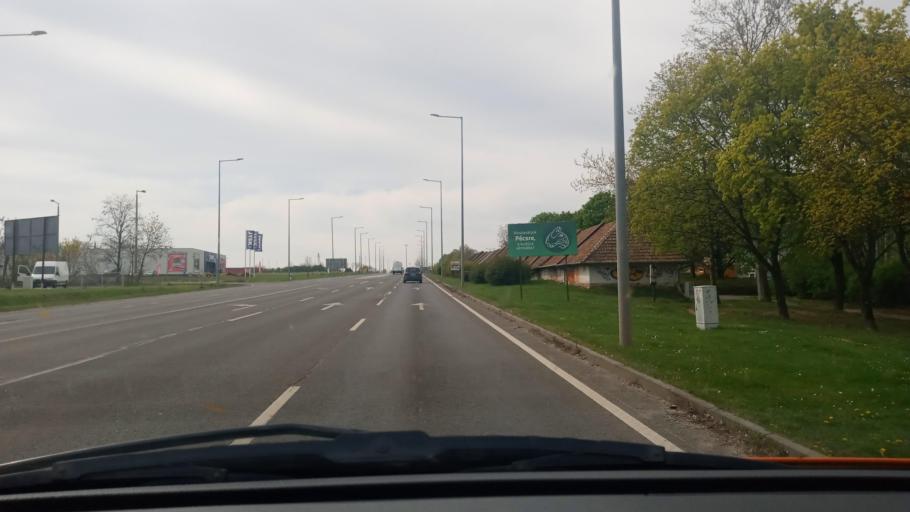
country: HU
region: Baranya
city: Pecs
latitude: 46.0427
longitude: 18.2321
